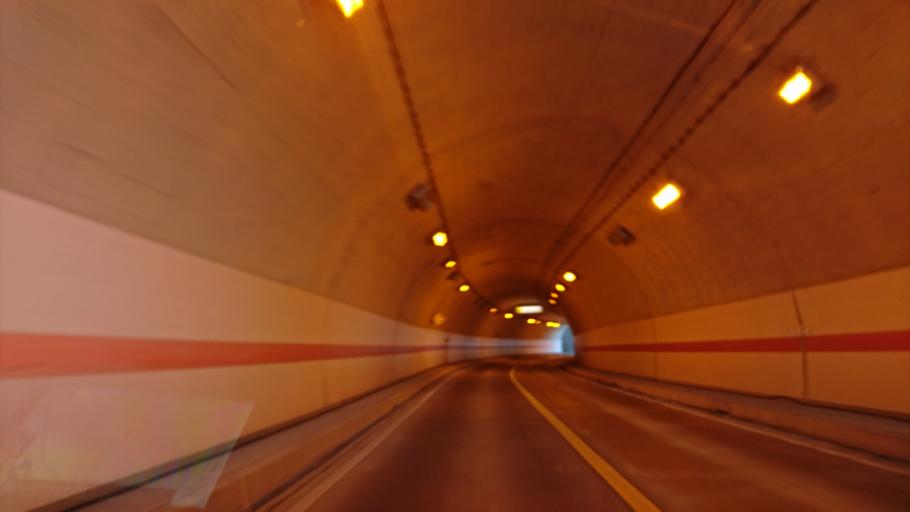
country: JP
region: Shizuoka
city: Yaizu
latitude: 34.8925
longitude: 138.3430
